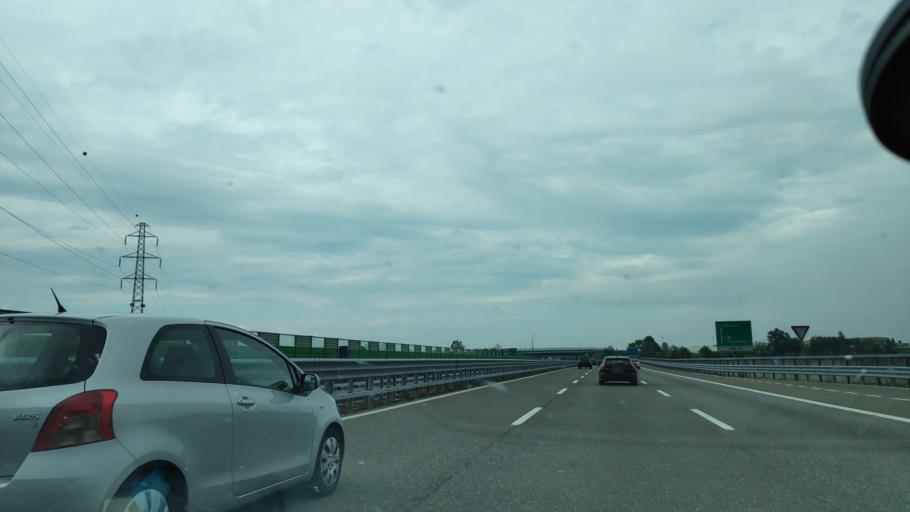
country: IT
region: Piedmont
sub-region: Provincia di Alessandria
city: Castelnuovo Scrivia
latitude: 44.9741
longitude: 8.8944
